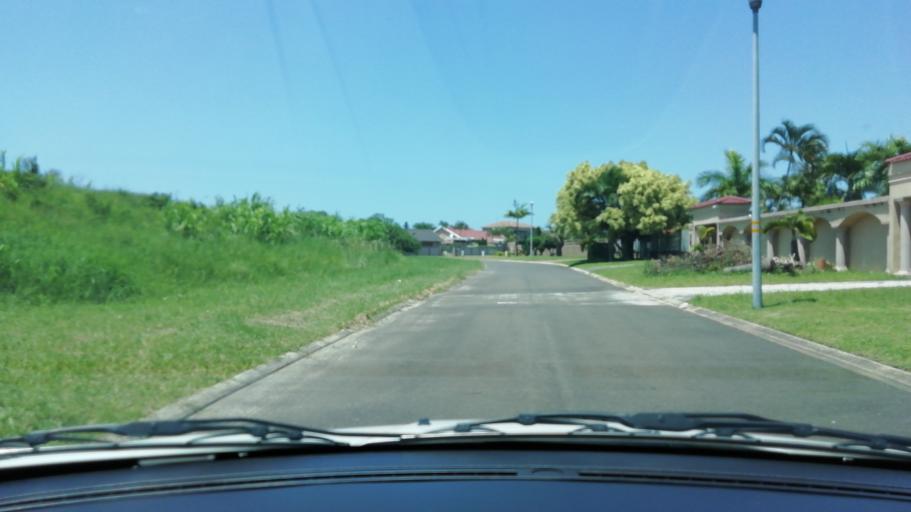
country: ZA
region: KwaZulu-Natal
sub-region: uThungulu District Municipality
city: Richards Bay
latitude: -28.7338
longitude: 32.0524
